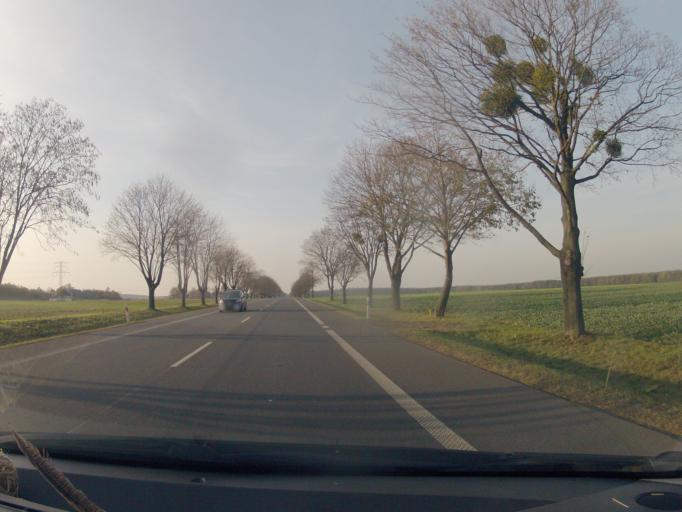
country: PL
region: Opole Voivodeship
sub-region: Powiat strzelecki
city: Strzelce Opolskie
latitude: 50.5295
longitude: 18.2658
